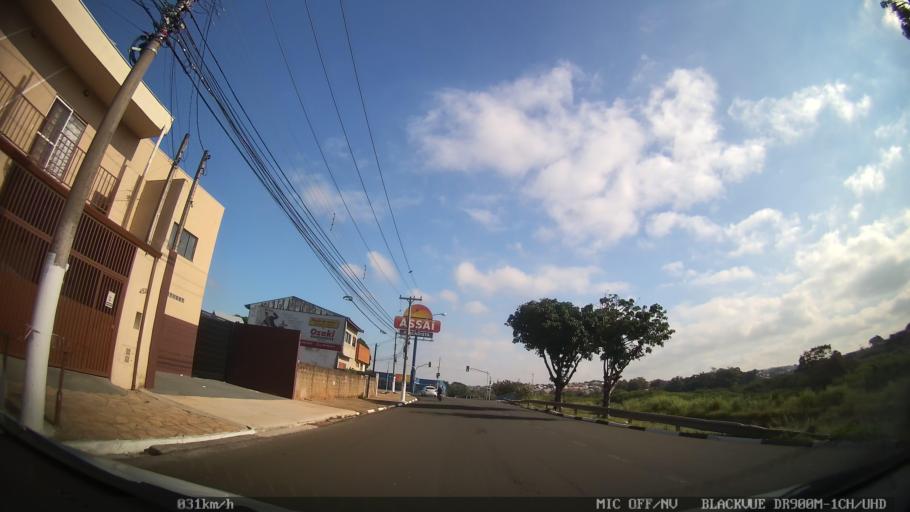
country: BR
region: Sao Paulo
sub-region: Hortolandia
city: Hortolandia
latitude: -22.8643
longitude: -47.2088
